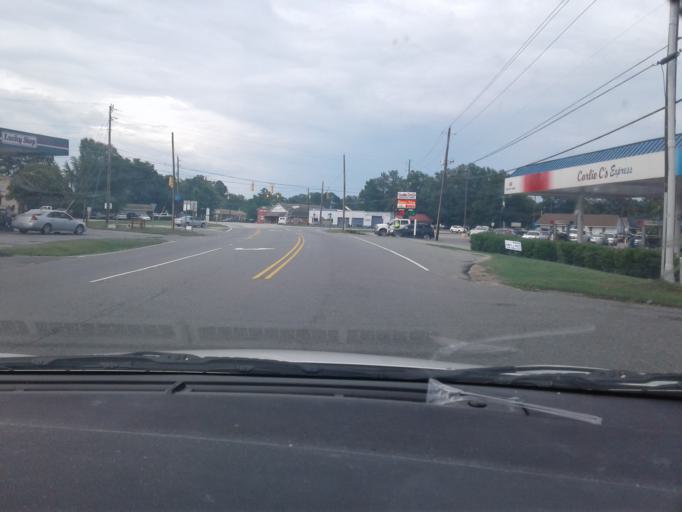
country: US
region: North Carolina
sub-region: Harnett County
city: Erwin
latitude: 35.3199
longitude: -78.6770
